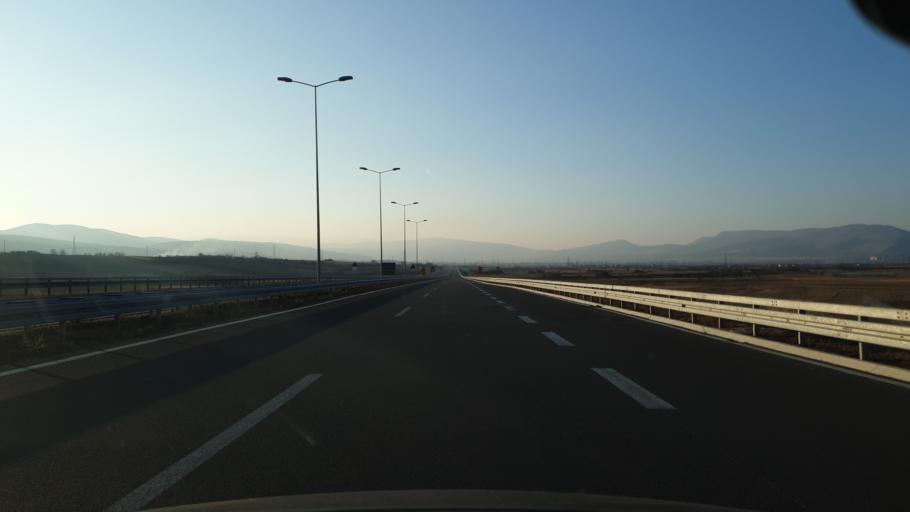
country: RS
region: Central Serbia
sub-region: Pirotski Okrug
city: Pirot
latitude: 43.1214
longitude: 22.6155
